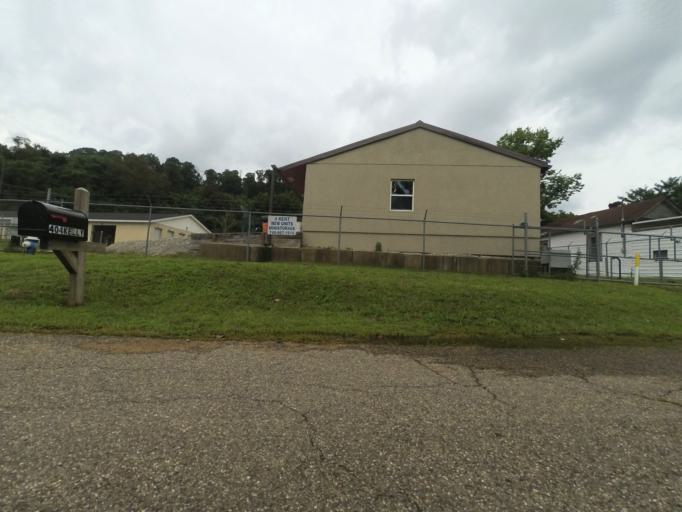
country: US
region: West Virginia
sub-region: Cabell County
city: Huntington
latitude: 38.4275
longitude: -82.4625
